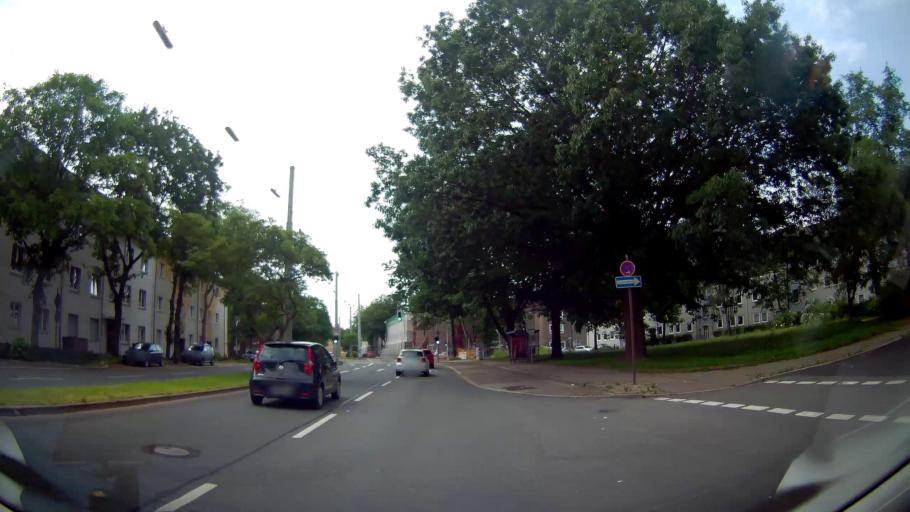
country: DE
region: North Rhine-Westphalia
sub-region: Regierungsbezirk Arnsberg
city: Herne
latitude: 51.5331
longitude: 7.2195
